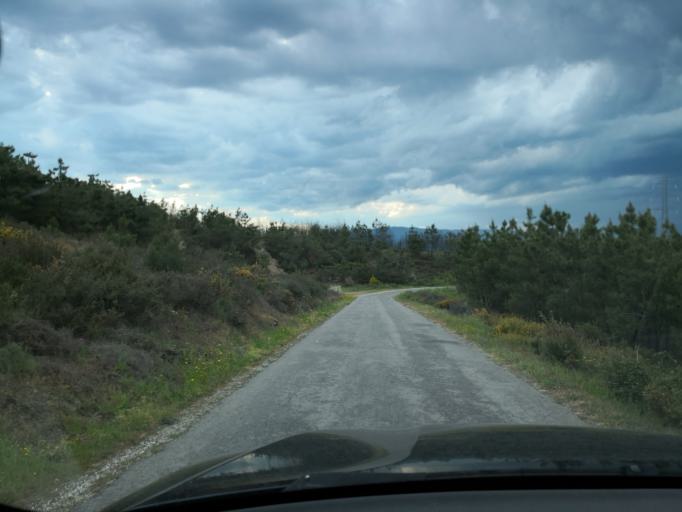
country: PT
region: Vila Real
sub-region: Sabrosa
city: Vilela
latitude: 41.2358
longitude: -7.6691
